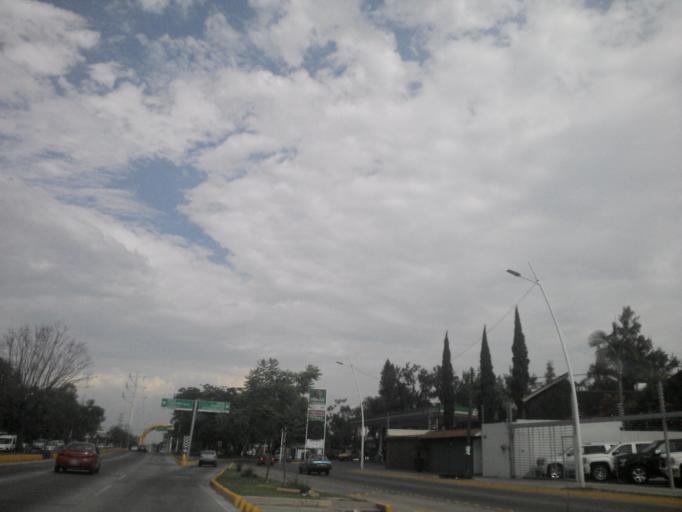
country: MX
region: Jalisco
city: Guadalajara
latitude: 20.6633
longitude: -103.3911
